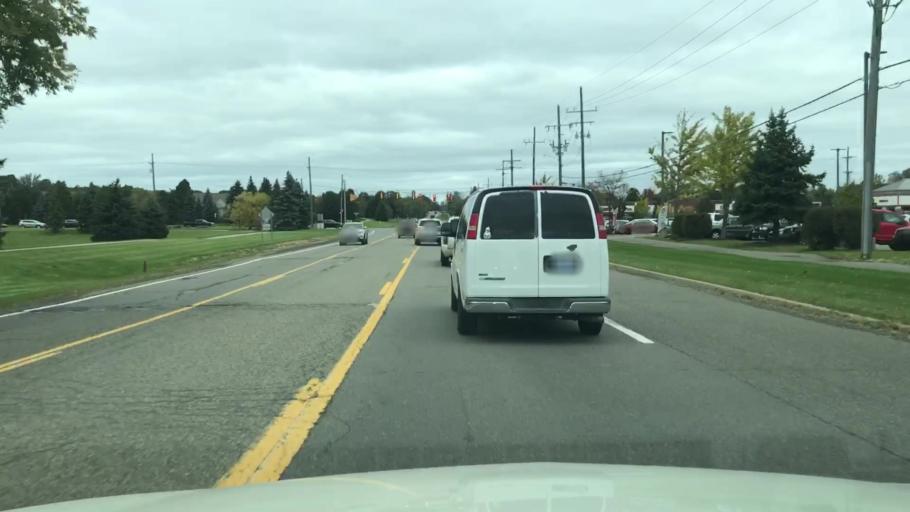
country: US
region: Michigan
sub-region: Oakland County
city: Rochester
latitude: 42.6952
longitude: -83.0948
